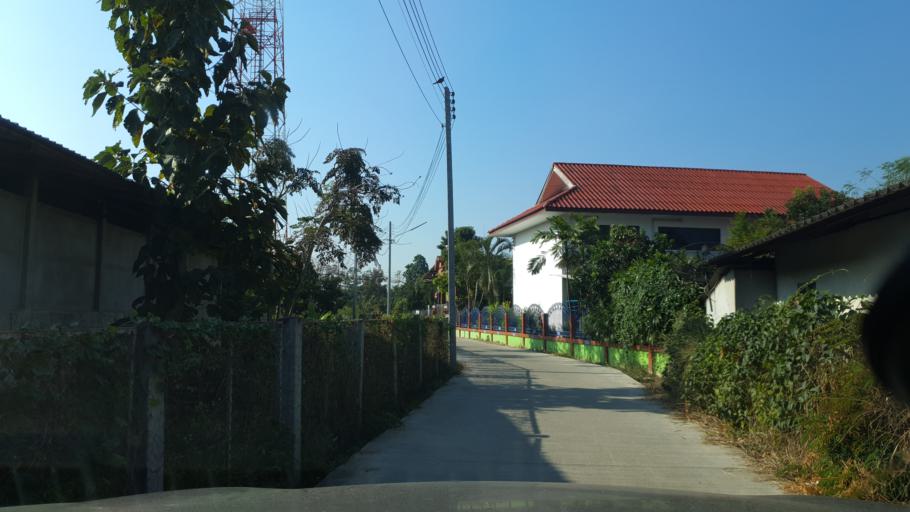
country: TH
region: Chiang Mai
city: San Kamphaeng
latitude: 18.6975
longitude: 99.1592
